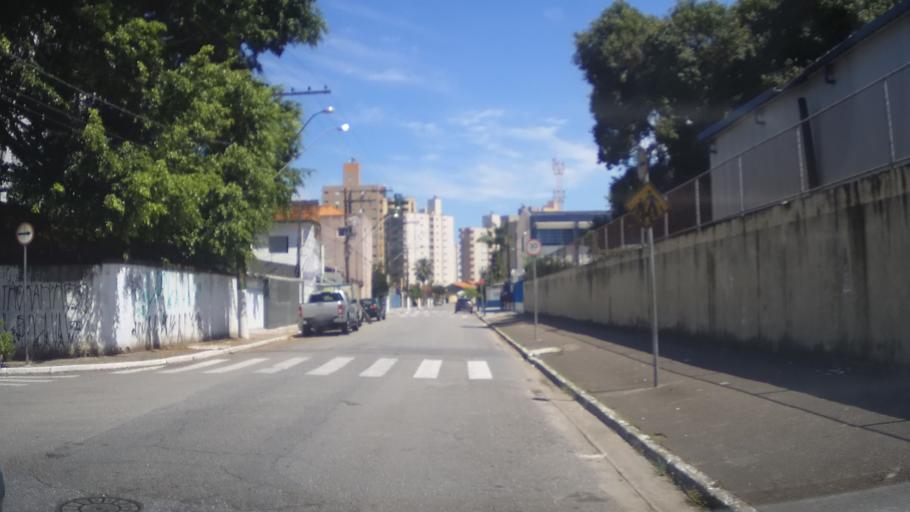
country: BR
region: Sao Paulo
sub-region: Praia Grande
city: Praia Grande
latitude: -24.0206
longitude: -46.4605
